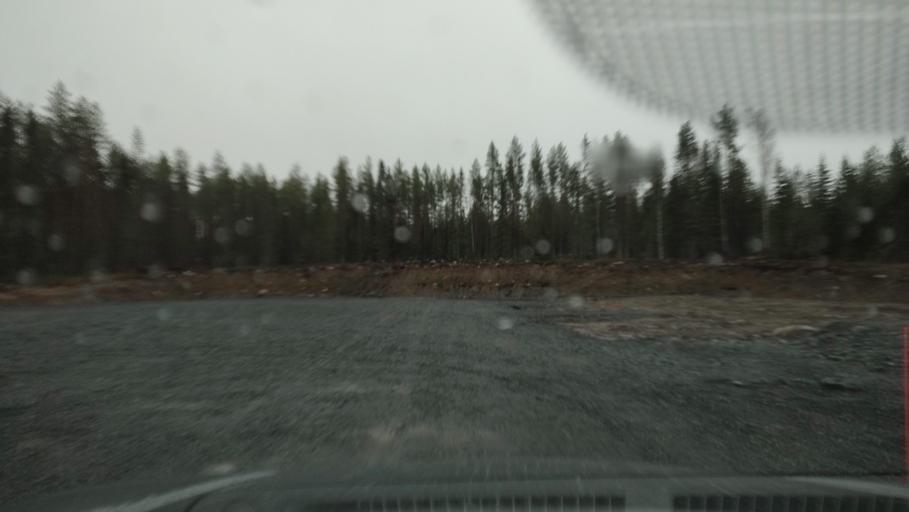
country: FI
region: Southern Ostrobothnia
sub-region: Suupohja
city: Karijoki
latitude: 62.1490
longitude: 21.6351
